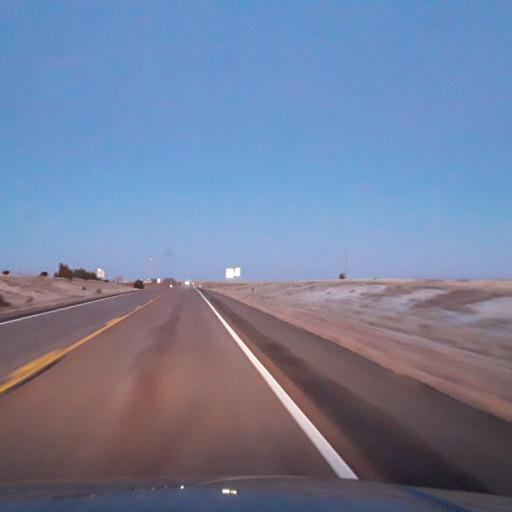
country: US
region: New Mexico
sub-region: Guadalupe County
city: Santa Rosa
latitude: 34.7745
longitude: -104.9570
